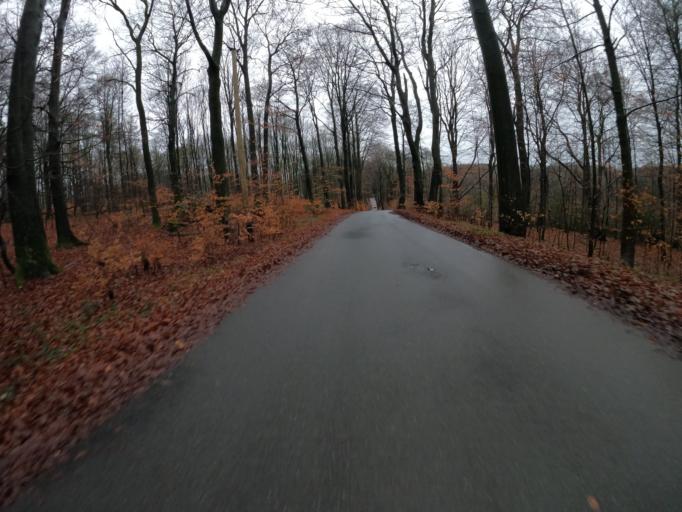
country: DE
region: North Rhine-Westphalia
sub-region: Regierungsbezirk Dusseldorf
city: Wuppertal
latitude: 51.2383
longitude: 7.1237
